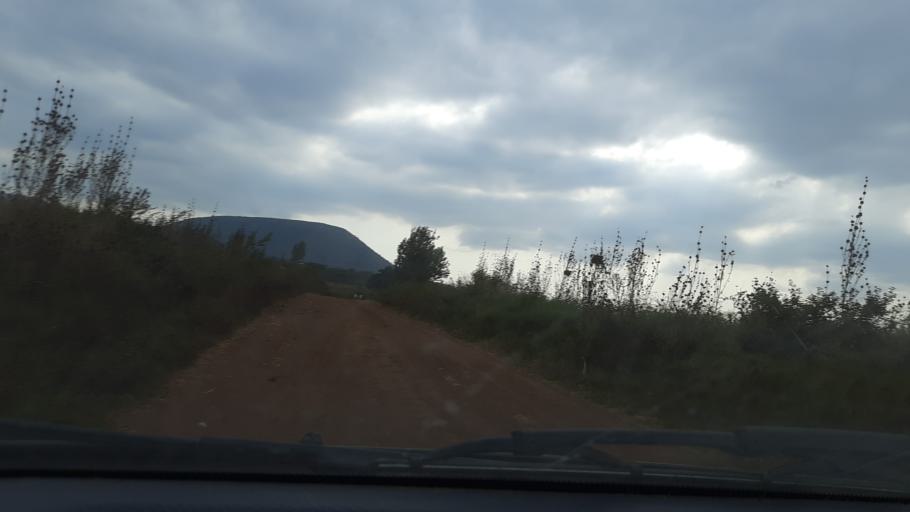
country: TZ
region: Arusha
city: Kingori
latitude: -2.8484
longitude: 37.2173
